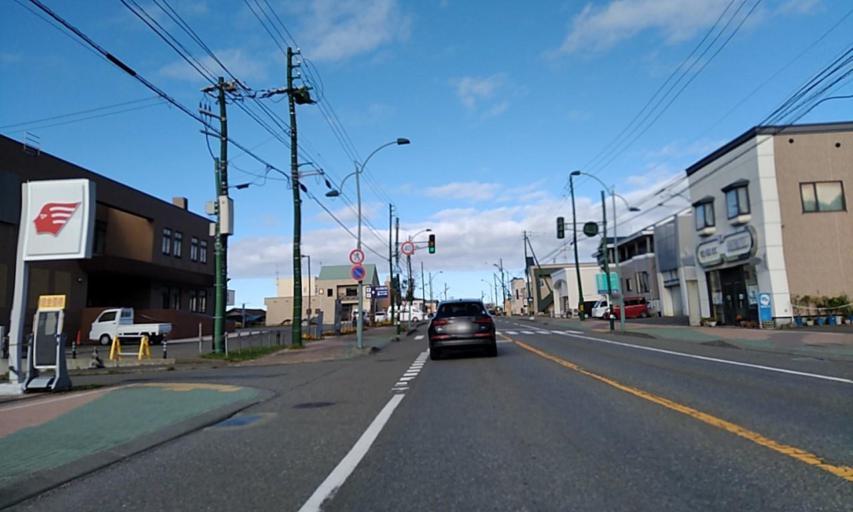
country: JP
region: Hokkaido
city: Shizunai-furukawacho
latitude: 42.2484
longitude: 142.5571
